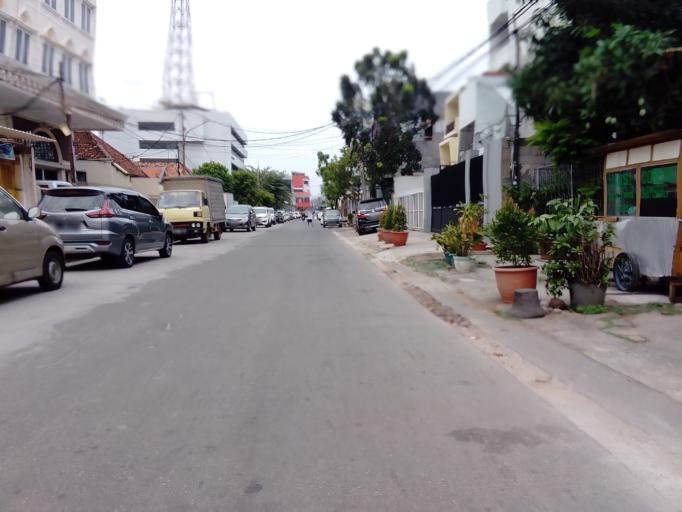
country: ID
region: Jakarta Raya
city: Jakarta
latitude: -6.1547
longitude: 106.8158
